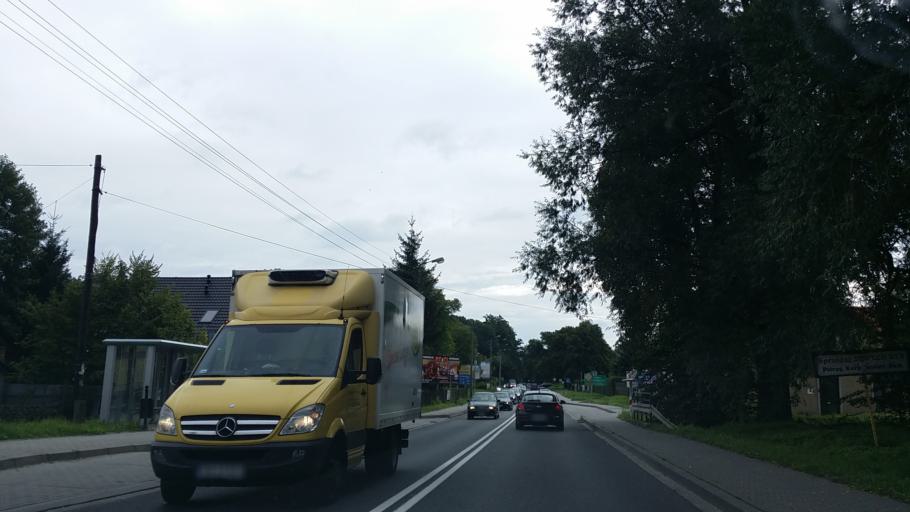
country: PL
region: Lesser Poland Voivodeship
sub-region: Powiat oswiecimski
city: Zator
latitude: 49.9981
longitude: 19.4298
